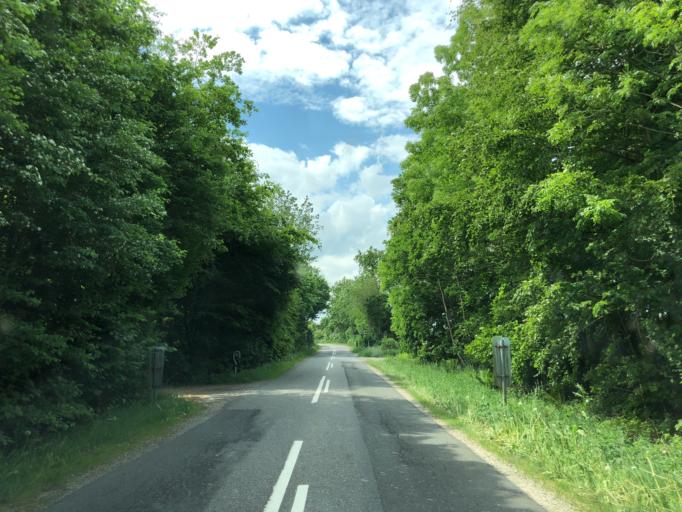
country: DK
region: Central Jutland
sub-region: Holstebro Kommune
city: Ulfborg
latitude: 56.3740
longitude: 8.3377
